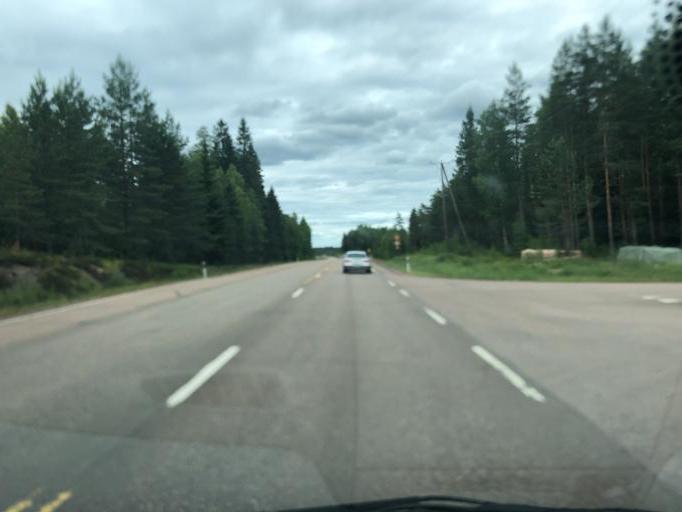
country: FI
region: Southern Savonia
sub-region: Mikkeli
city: Maentyharju
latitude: 61.0676
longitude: 27.0553
